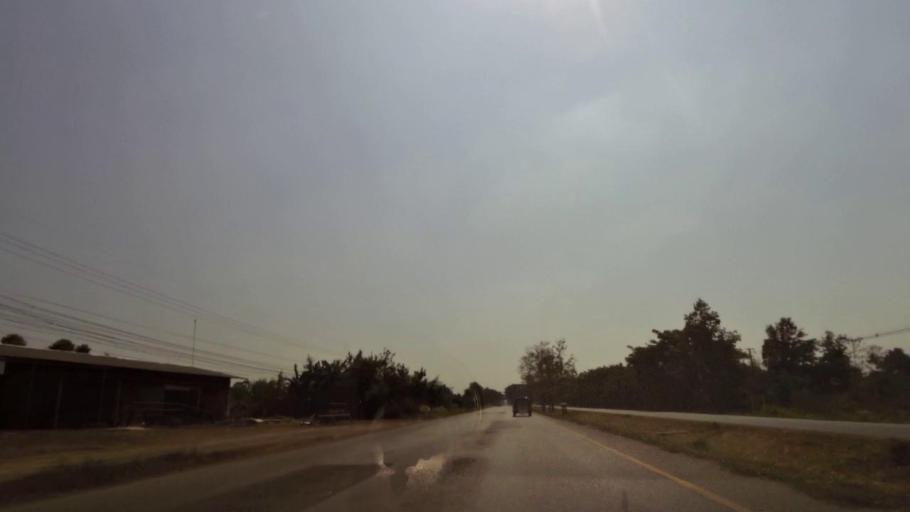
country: TH
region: Phichit
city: Bueng Na Rang
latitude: 16.3423
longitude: 100.1283
